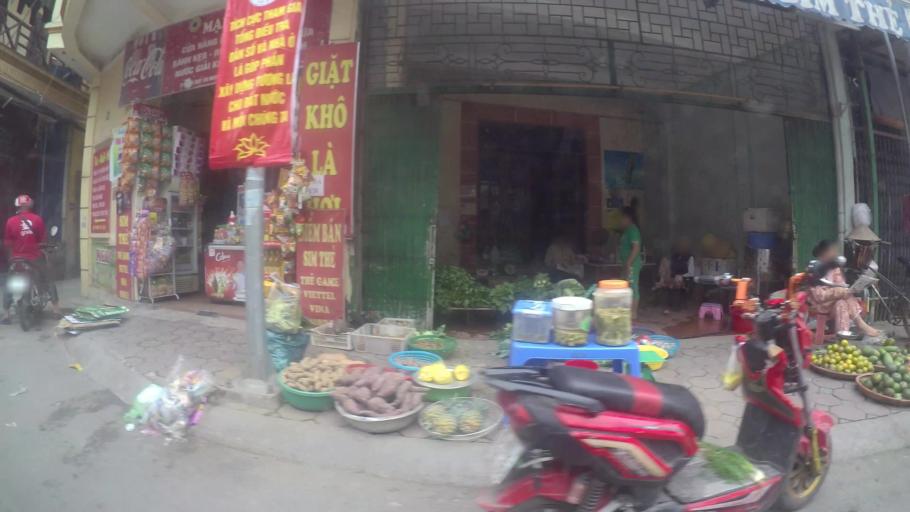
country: VN
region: Ha Noi
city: Dong Da
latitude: 21.0381
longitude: 105.8251
